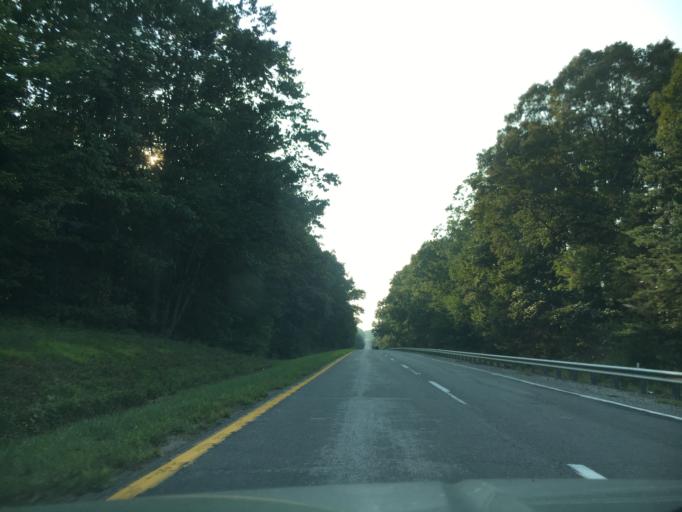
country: US
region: Virginia
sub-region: Appomattox County
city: Appomattox
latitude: 37.2682
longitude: -78.6616
